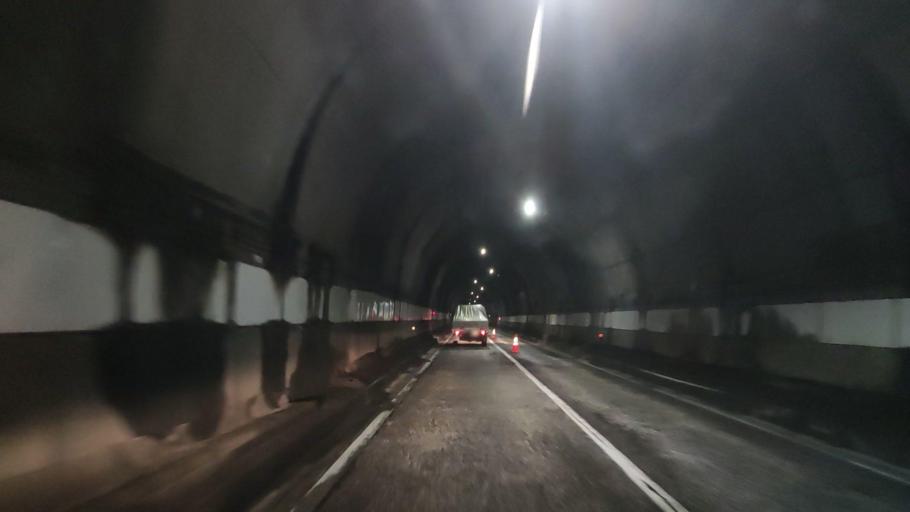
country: JP
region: Nagano
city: Toyoshina
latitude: 36.1538
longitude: 137.6808
